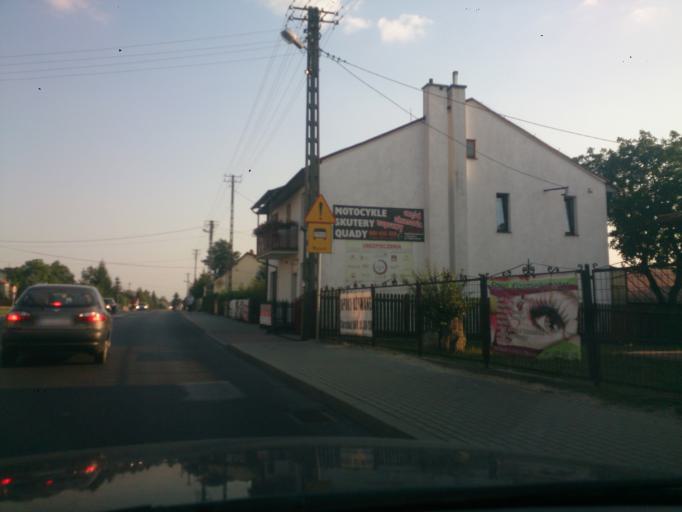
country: PL
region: Subcarpathian Voivodeship
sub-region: Powiat kolbuszowski
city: Majdan Krolewski
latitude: 50.3751
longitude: 21.7460
